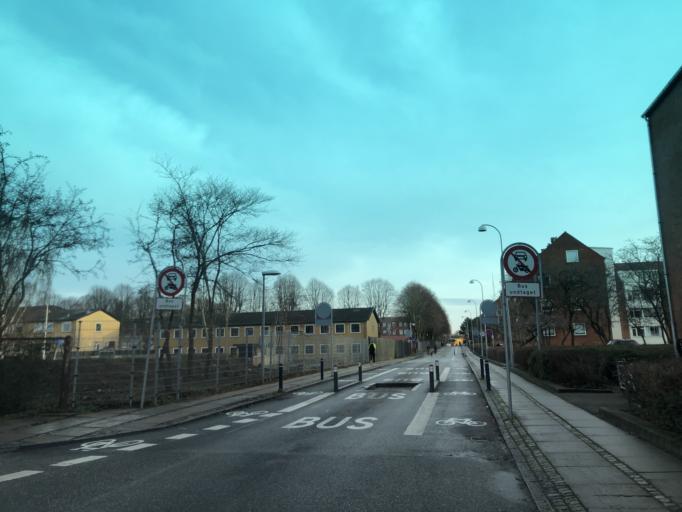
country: DK
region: Capital Region
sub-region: Hvidovre Kommune
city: Hvidovre
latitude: 55.6480
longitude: 12.4722
